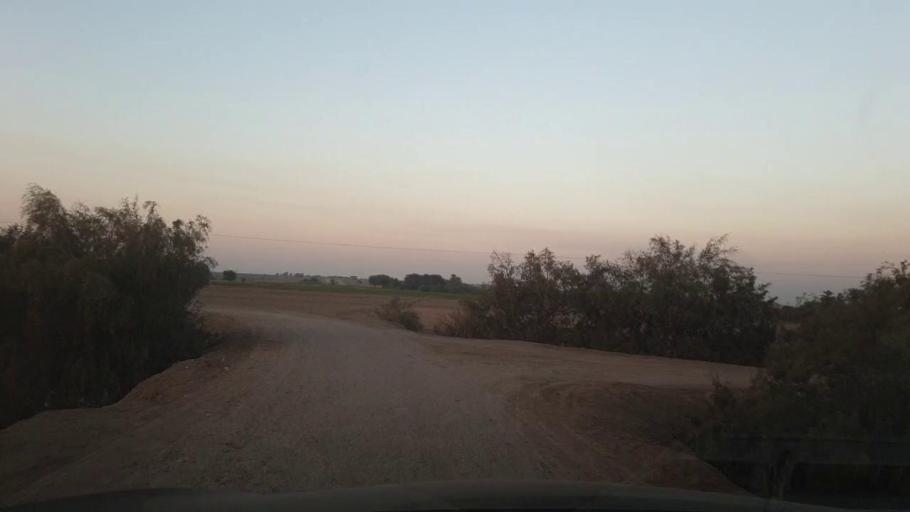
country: PK
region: Sindh
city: Ubauro
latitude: 28.1748
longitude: 69.6354
